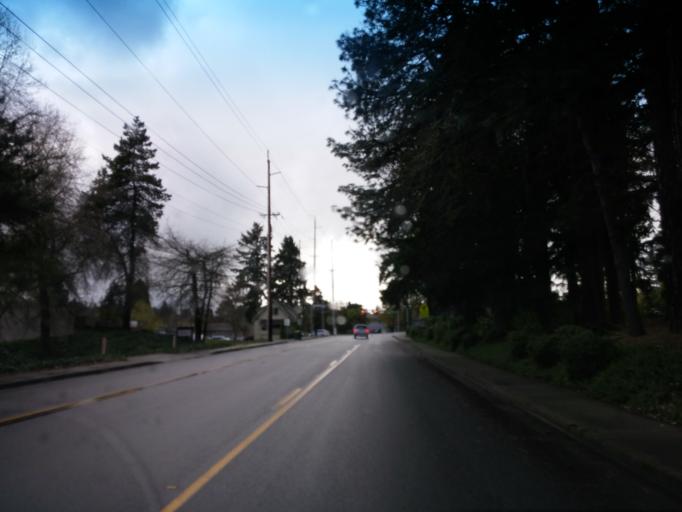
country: US
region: Oregon
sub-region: Washington County
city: Aloha
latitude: 45.5053
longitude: -122.8501
